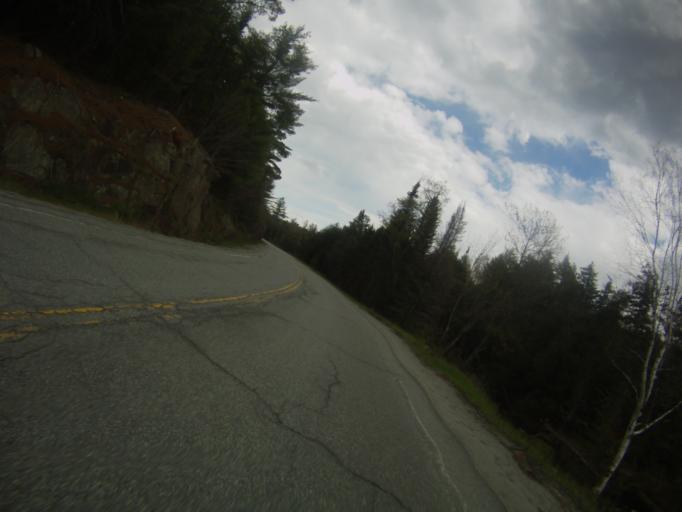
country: US
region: New York
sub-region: Essex County
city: Mineville
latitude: 44.0776
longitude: -73.6058
